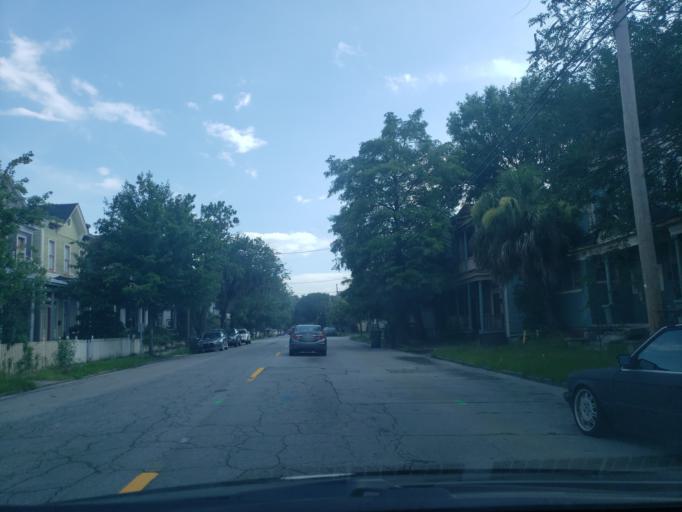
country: US
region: Georgia
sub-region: Chatham County
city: Savannah
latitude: 32.0567
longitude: -81.1027
